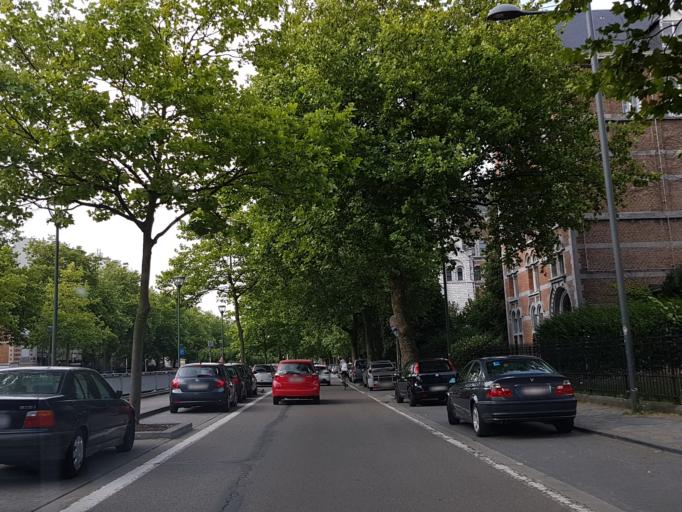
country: BE
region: Brussels Capital
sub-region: Bruxelles-Capitale
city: Brussels
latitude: 50.8339
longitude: 4.4060
